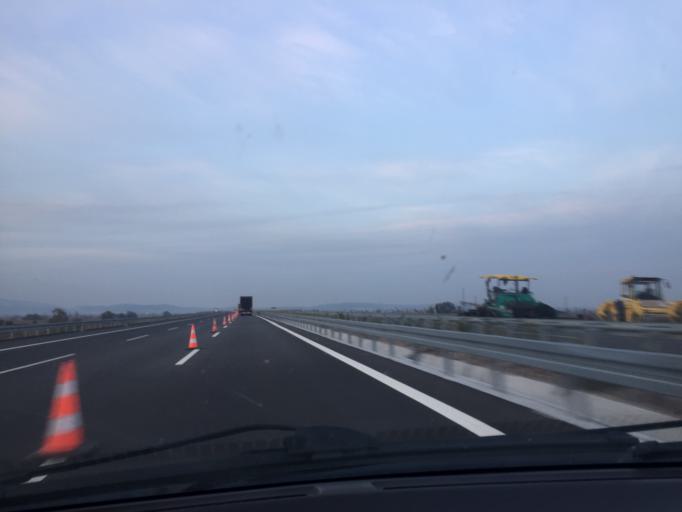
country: TR
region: Manisa
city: Halitpasa
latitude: 38.7254
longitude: 27.6535
